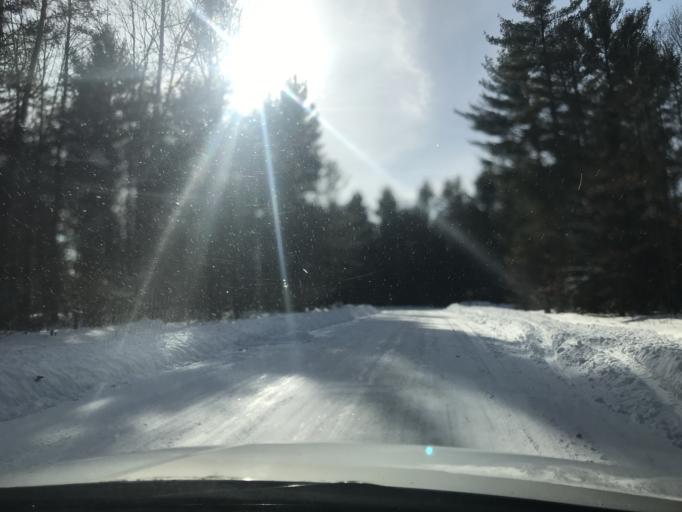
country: US
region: Wisconsin
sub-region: Oconto County
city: Gillett
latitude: 45.1374
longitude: -88.2499
